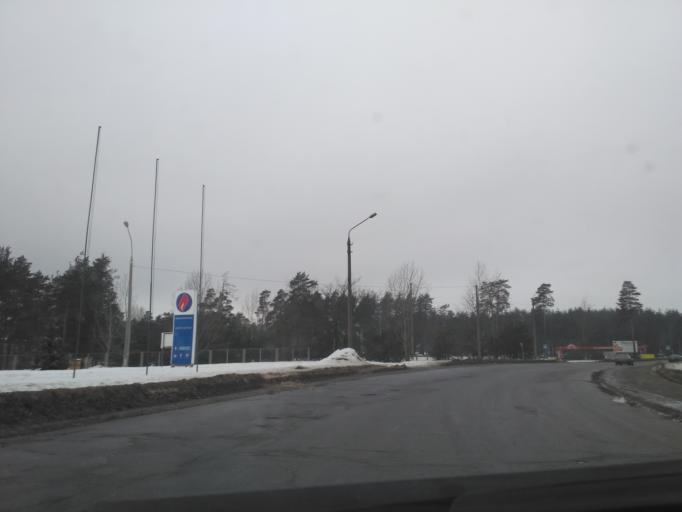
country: BY
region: Minsk
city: Horad Barysaw
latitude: 54.1997
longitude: 28.4861
